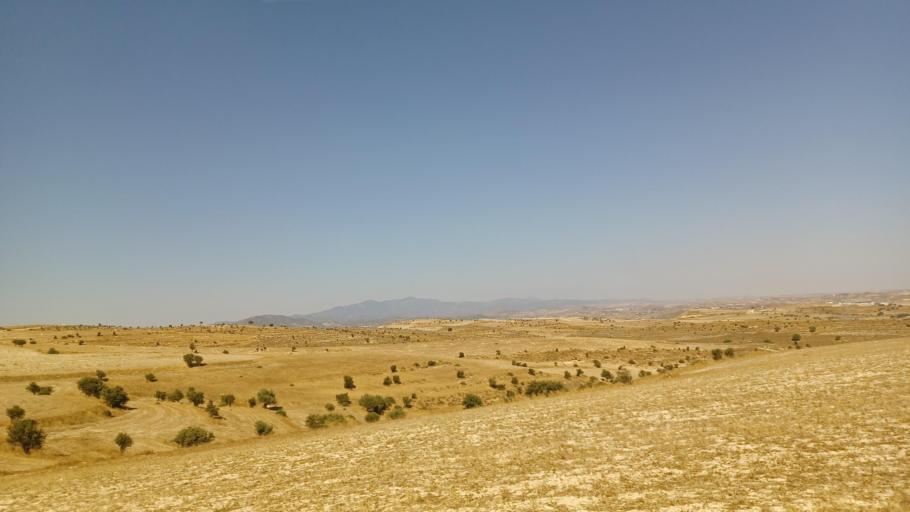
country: CY
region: Lefkosia
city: Lympia
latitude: 34.9794
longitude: 33.4851
